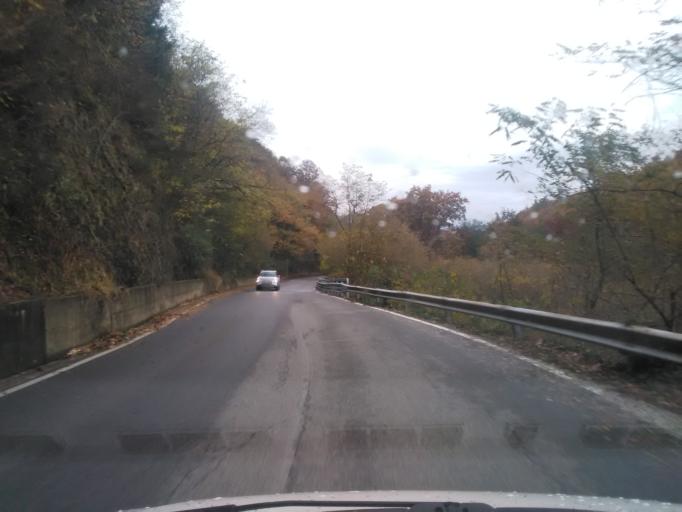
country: IT
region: Piedmont
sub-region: Provincia di Novara
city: Pogno
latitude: 45.7669
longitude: 8.3858
